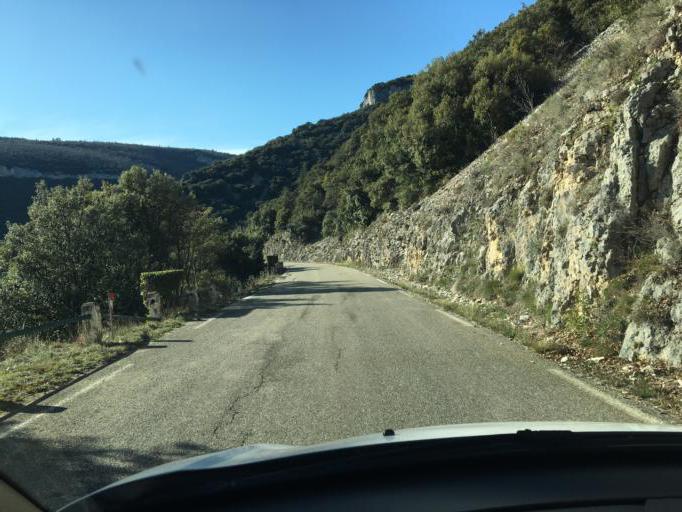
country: FR
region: Provence-Alpes-Cote d'Azur
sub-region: Departement du Vaucluse
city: Villes-sur-Auzon
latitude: 44.0649
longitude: 5.3134
